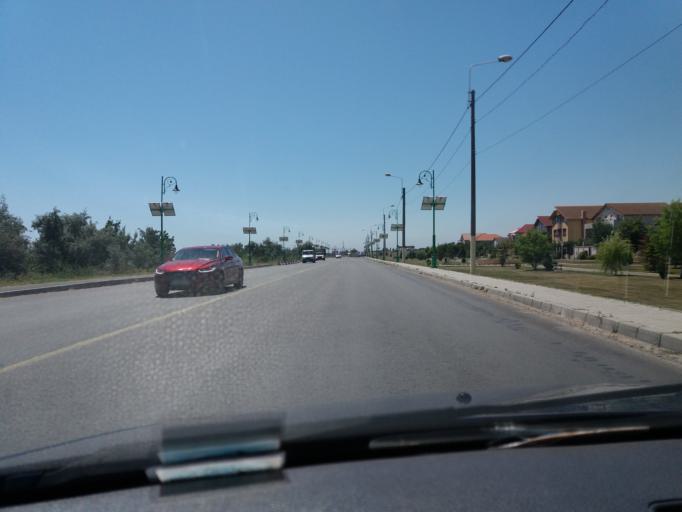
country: RO
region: Constanta
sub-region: Comuna Navodari
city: Navodari
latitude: 44.3111
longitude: 28.6161
